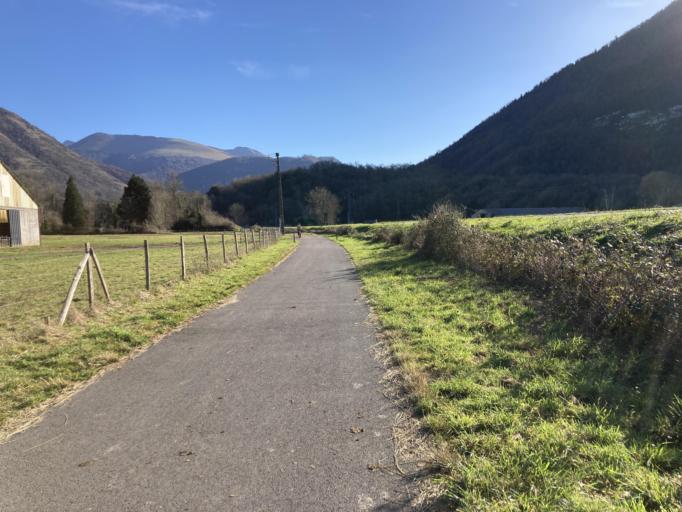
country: FR
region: Aquitaine
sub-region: Departement des Pyrenees-Atlantiques
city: Louvie-Juzon
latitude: 43.0931
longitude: -0.4327
